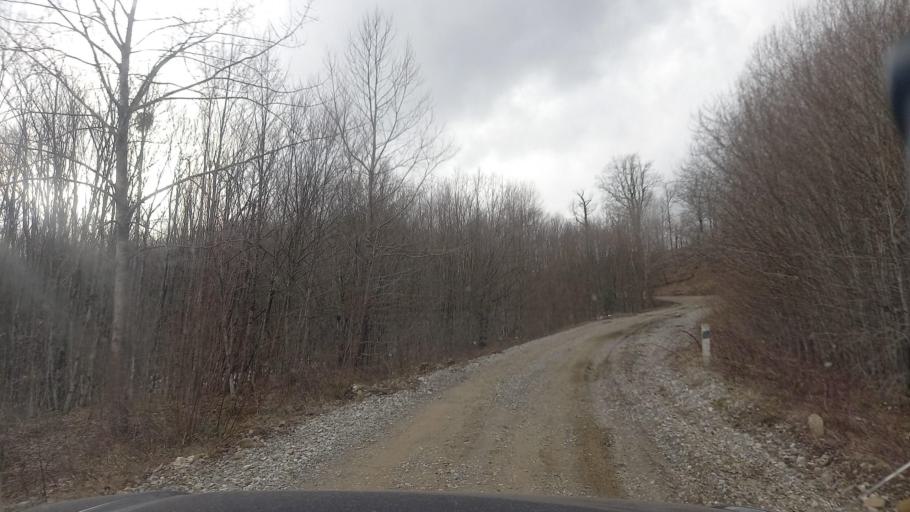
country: RU
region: Krasnodarskiy
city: Dzhubga
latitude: 44.5252
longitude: 38.7750
